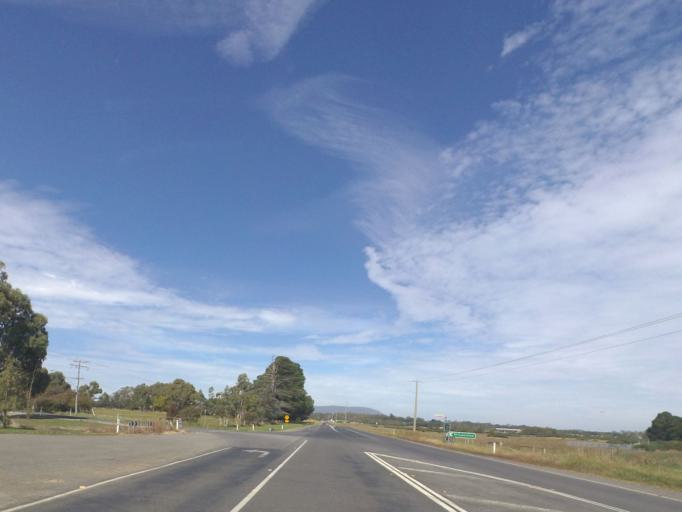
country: AU
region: Victoria
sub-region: Mount Alexander
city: Castlemaine
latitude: -37.2848
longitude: 144.4998
